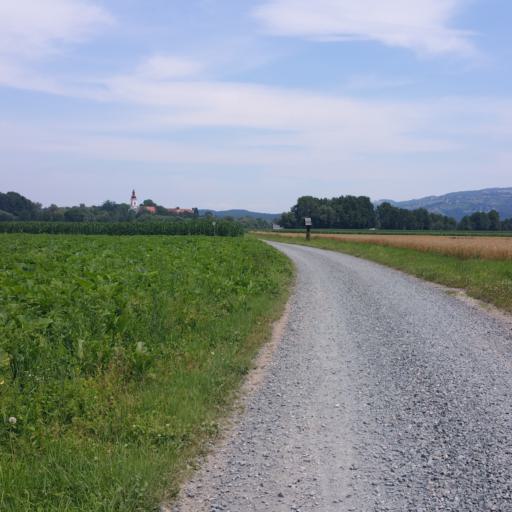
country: AT
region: Styria
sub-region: Politischer Bezirk Leibnitz
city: Gleinstatten
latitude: 46.7433
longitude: 15.3624
